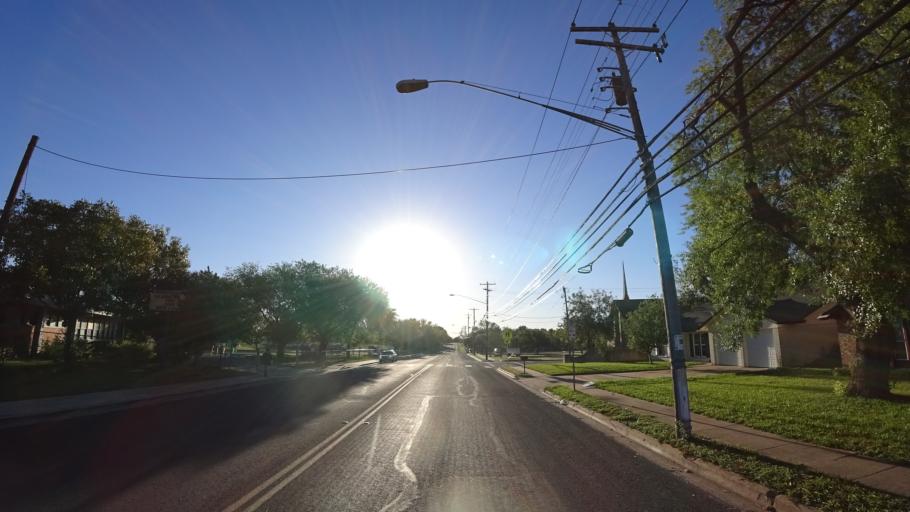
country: US
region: Texas
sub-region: Travis County
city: Austin
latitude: 30.3025
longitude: -97.6772
